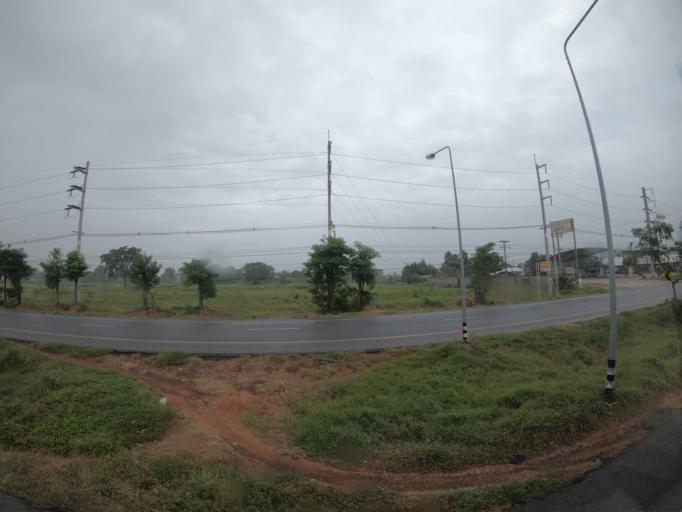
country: TH
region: Maha Sarakham
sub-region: Amphoe Borabue
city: Borabue
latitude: 16.0492
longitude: 103.0967
